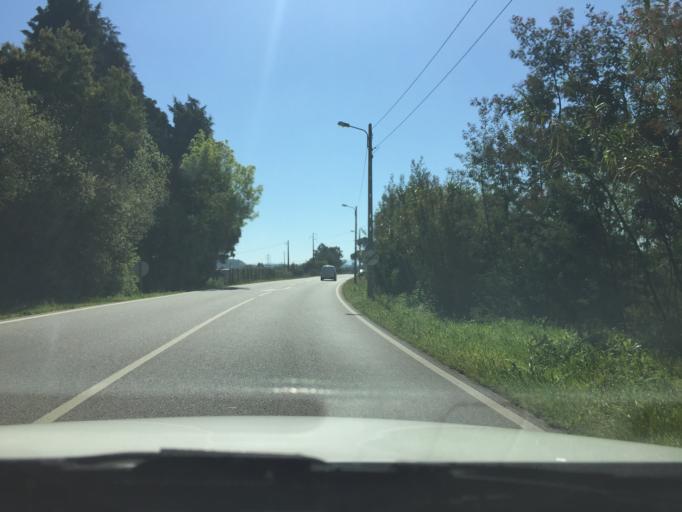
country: PT
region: Aveiro
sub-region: Anadia
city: Arcos
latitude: 40.4470
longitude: -8.4621
